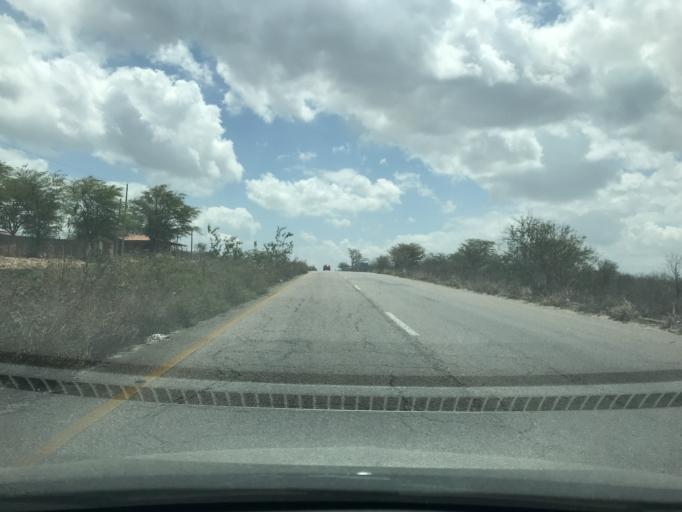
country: BR
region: Pernambuco
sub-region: Caruaru
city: Caruaru
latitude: -8.2981
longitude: -35.9008
